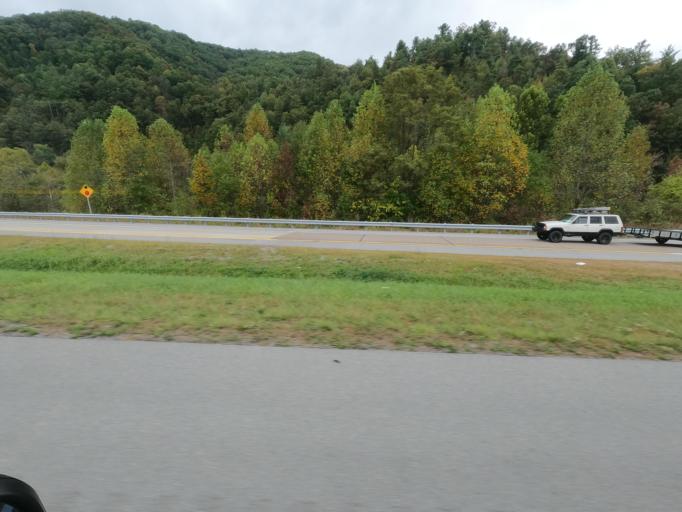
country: US
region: Tennessee
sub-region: Unicoi County
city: Banner Hill
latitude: 36.0875
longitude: -82.4892
